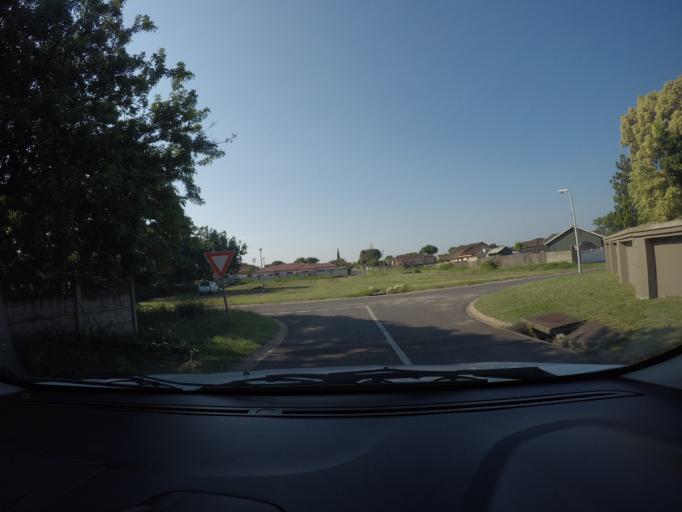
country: ZA
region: KwaZulu-Natal
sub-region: uThungulu District Municipality
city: Richards Bay
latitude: -28.7165
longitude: 32.0330
